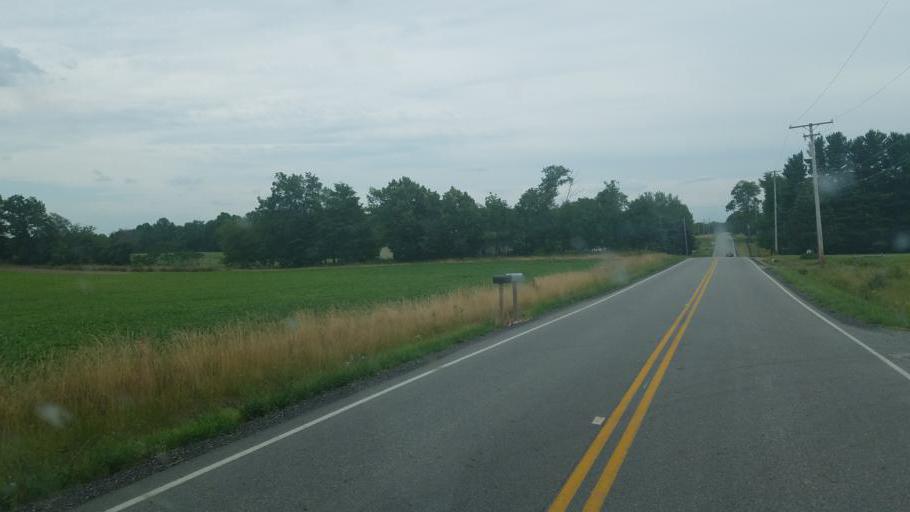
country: US
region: Ohio
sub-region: Geauga County
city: Burton
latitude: 41.4919
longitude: -81.1177
